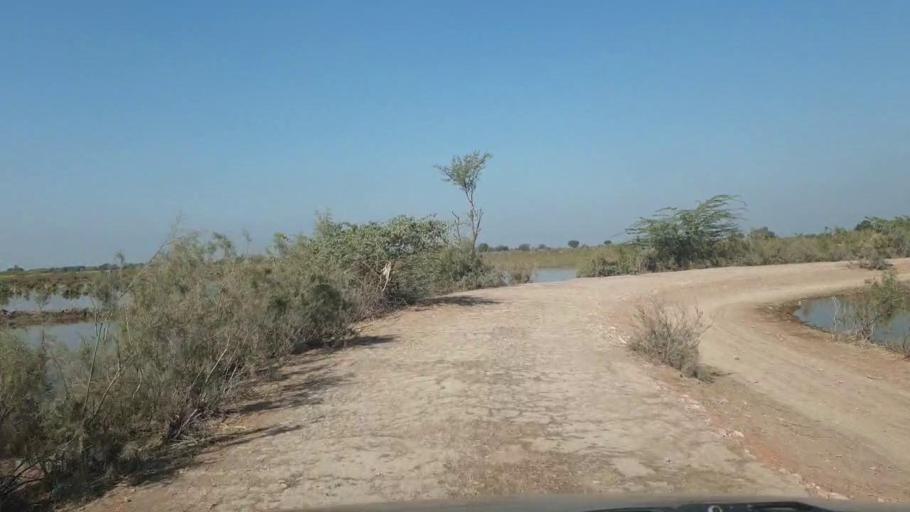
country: PK
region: Sindh
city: Bhit Shah
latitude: 25.8762
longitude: 68.5264
